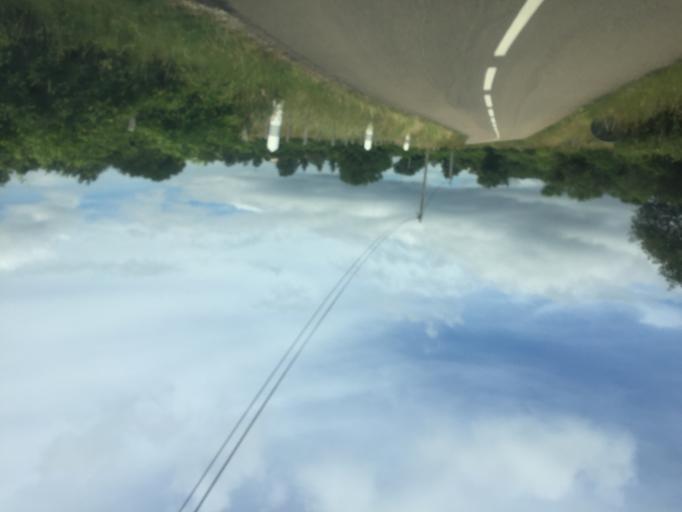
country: FR
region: Rhone-Alpes
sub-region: Departement de l'Ardeche
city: Villeneuve-de-Berg
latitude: 44.6232
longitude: 4.5449
